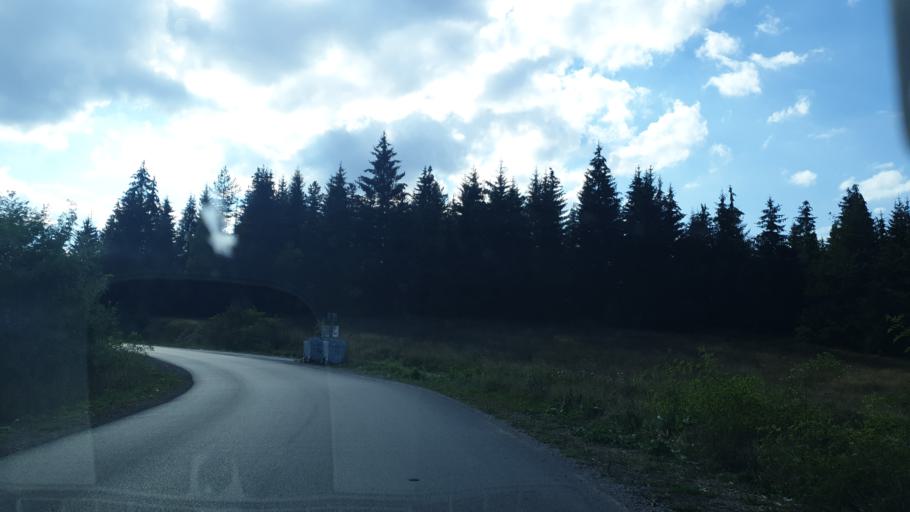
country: RS
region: Central Serbia
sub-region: Zlatiborski Okrug
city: Nova Varos
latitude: 43.4308
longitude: 19.8892
